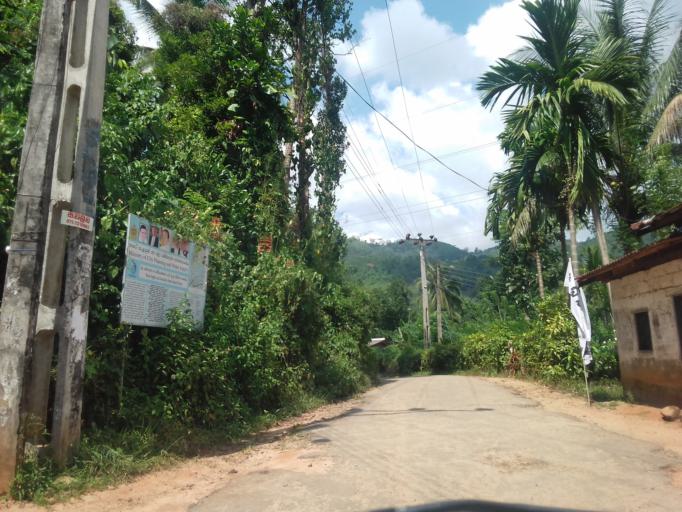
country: LK
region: Central
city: Gampola
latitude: 7.0143
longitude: 80.3548
